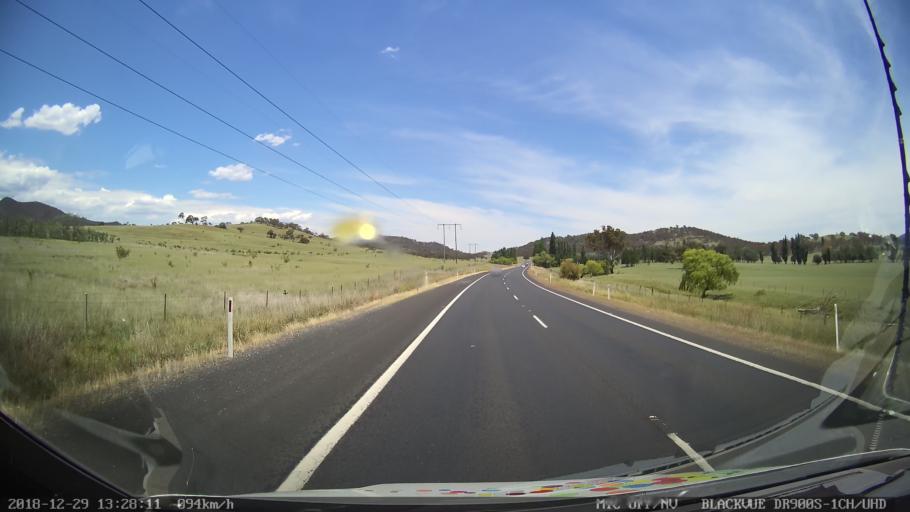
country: AU
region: New South Wales
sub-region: Cooma-Monaro
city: Cooma
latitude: -35.8720
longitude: 149.1614
